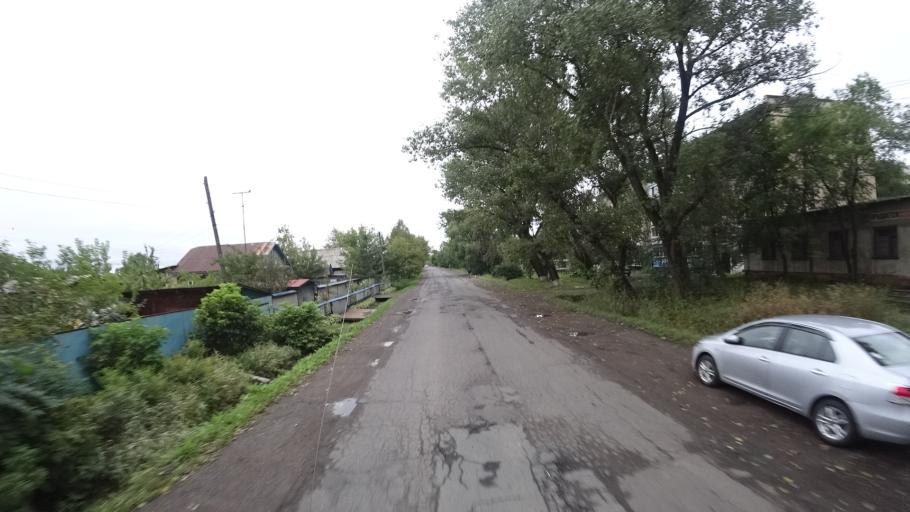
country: RU
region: Primorskiy
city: Chernigovka
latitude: 44.3361
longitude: 132.5307
